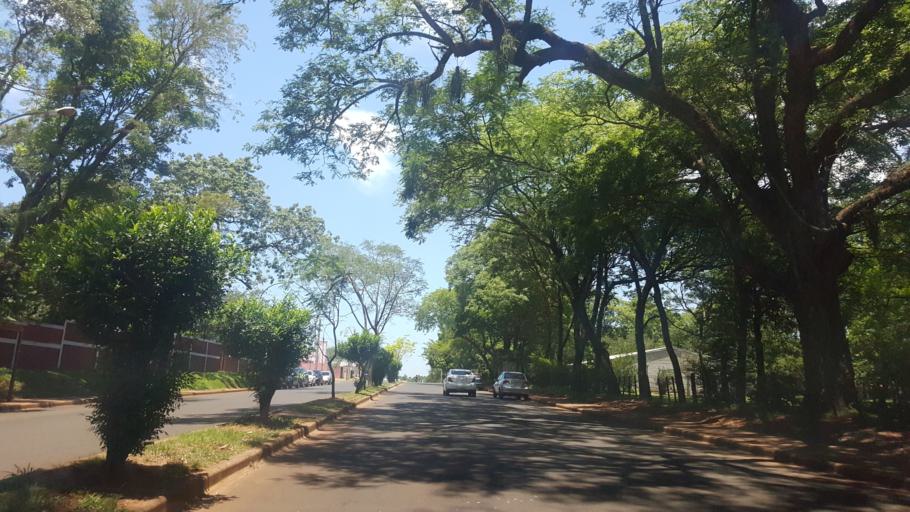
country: AR
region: Misiones
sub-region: Departamento de Capital
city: Posadas
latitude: -27.3587
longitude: -55.9381
